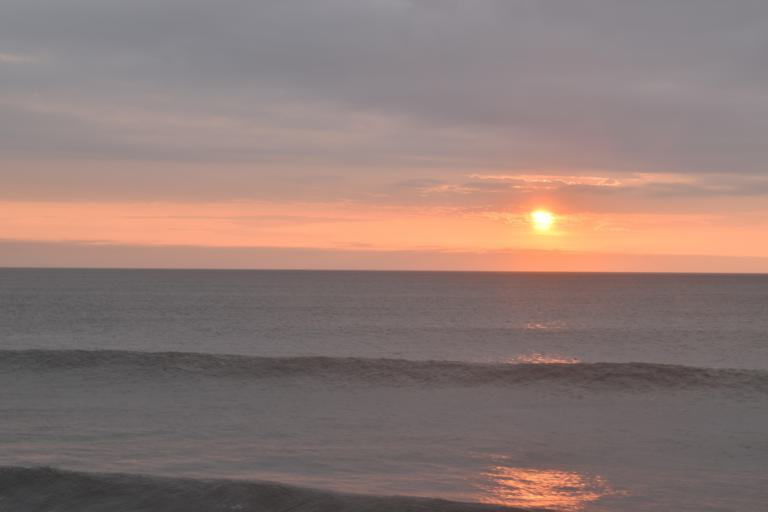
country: PE
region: La Libertad
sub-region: Ascope
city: Paijan
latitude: -7.7004
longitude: -79.4387
